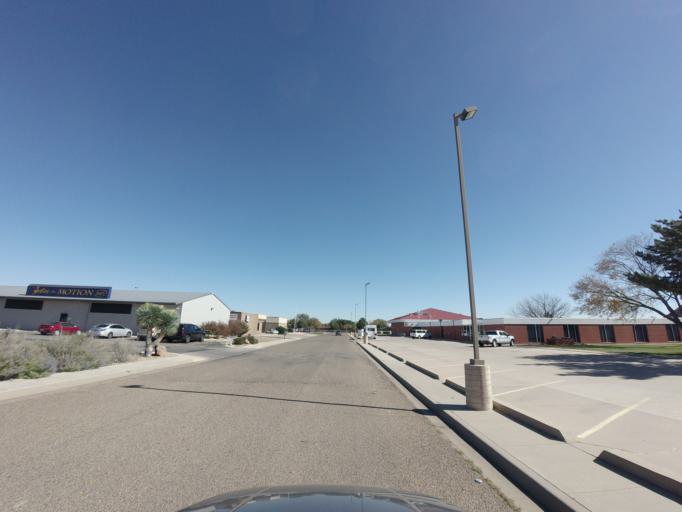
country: US
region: New Mexico
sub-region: Curry County
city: Clovis
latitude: 34.4230
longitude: -103.1945
